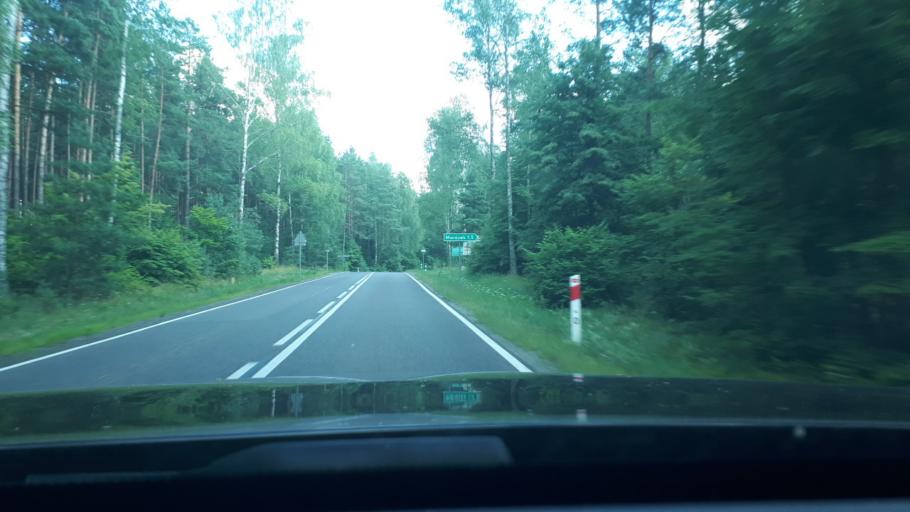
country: PL
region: Warmian-Masurian Voivodeship
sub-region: Powiat olsztynski
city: Stawiguda
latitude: 53.5305
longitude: 20.4398
